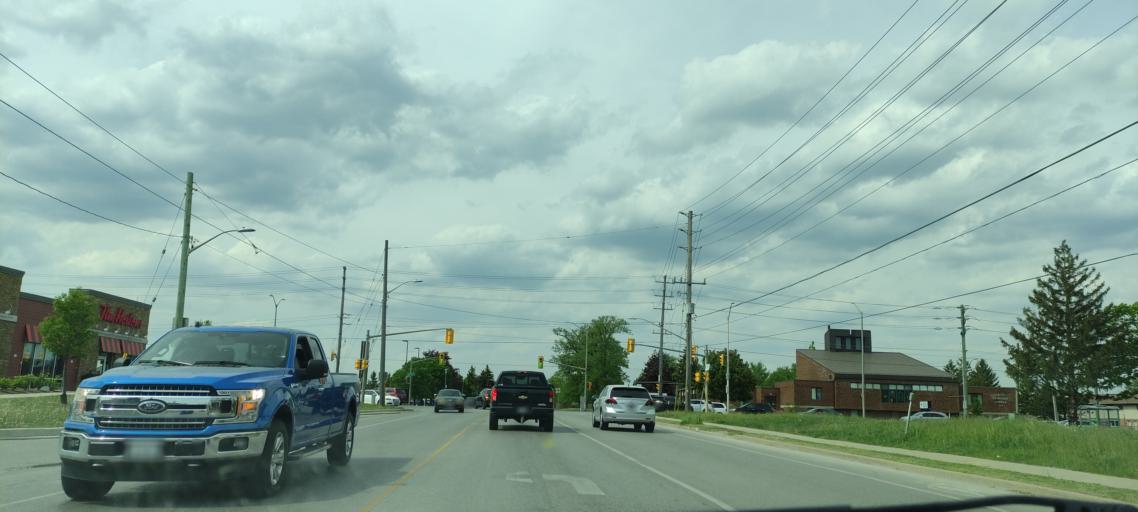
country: CA
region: Ontario
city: London
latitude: 42.9405
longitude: -81.2519
